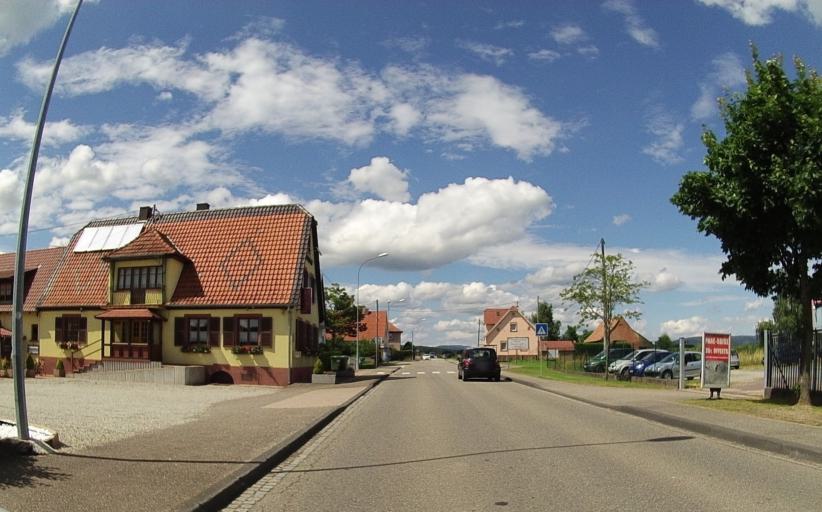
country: FR
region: Alsace
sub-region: Departement du Bas-Rhin
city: Eschbach
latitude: 48.8908
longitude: 7.7471
